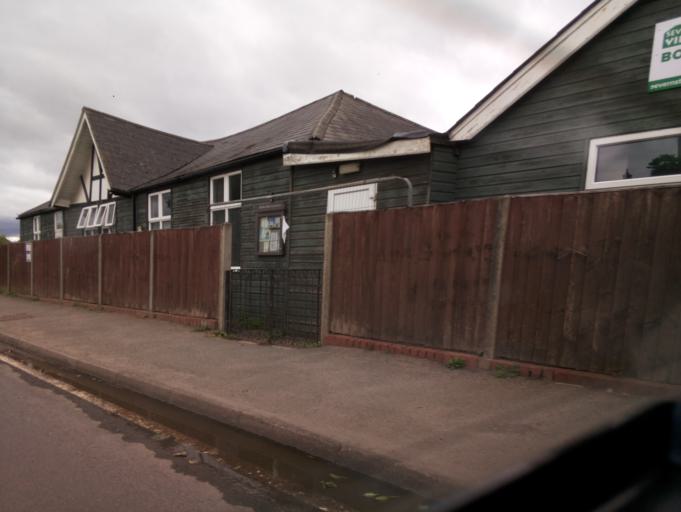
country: GB
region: England
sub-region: Worcestershire
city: Upton upon Severn
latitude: 52.0965
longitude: -2.2096
